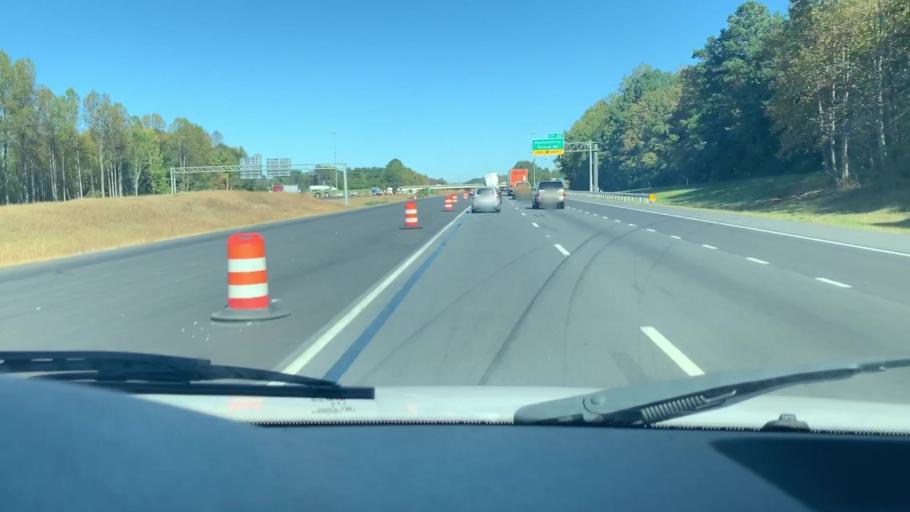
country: US
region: North Carolina
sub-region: Mecklenburg County
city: Huntersville
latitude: 35.4034
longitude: -80.8564
